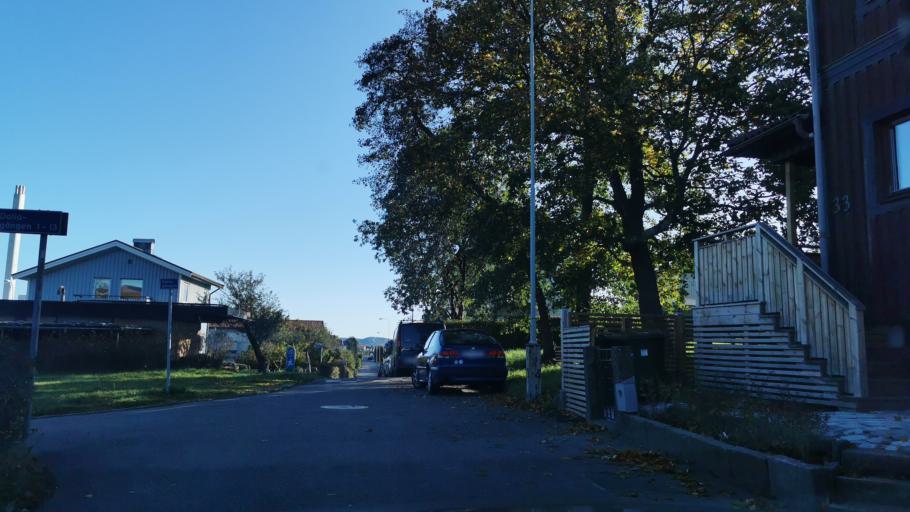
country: SE
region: Vaestra Goetaland
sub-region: Goteborg
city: Eriksbo
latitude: 57.7278
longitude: 12.0462
